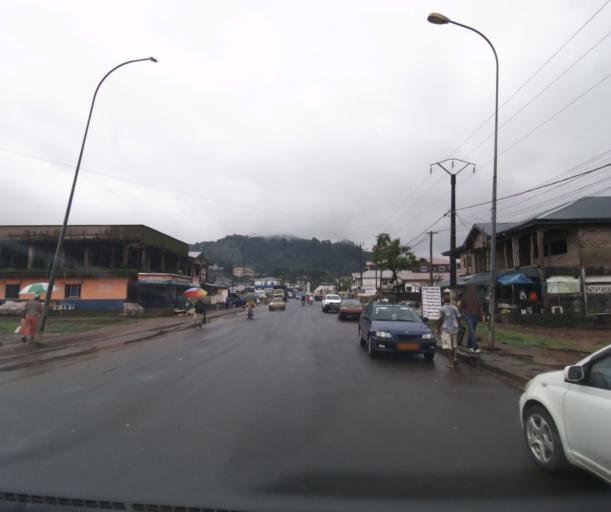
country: CM
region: South-West Province
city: Limbe
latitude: 4.0157
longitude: 9.2108
